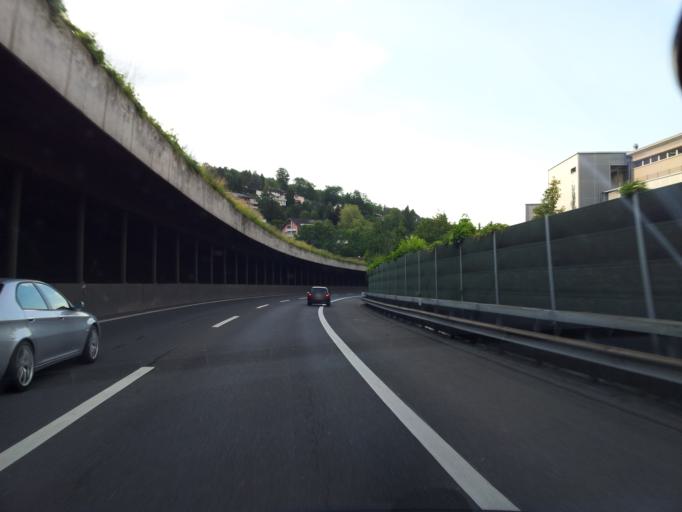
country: CH
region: Nidwalden
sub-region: Nidwalden
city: Hergiswil
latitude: 46.9918
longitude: 8.3079
